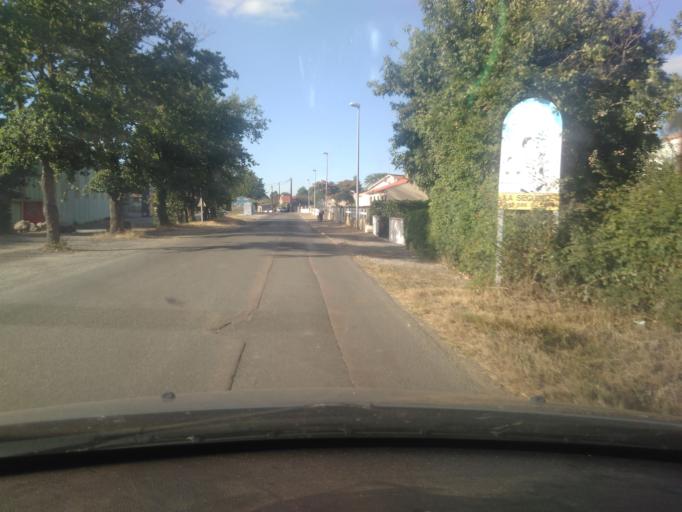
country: FR
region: Pays de la Loire
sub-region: Departement de la Vendee
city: Saint-Florent-des-Bois
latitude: 46.5899
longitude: -1.3151
